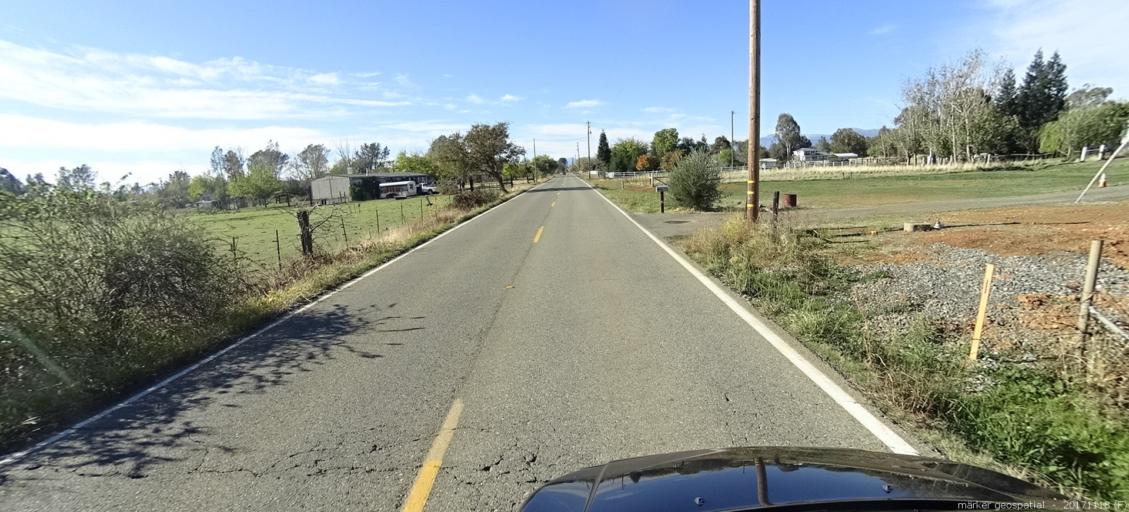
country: US
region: California
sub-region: Shasta County
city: Anderson
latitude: 40.4391
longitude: -122.3952
